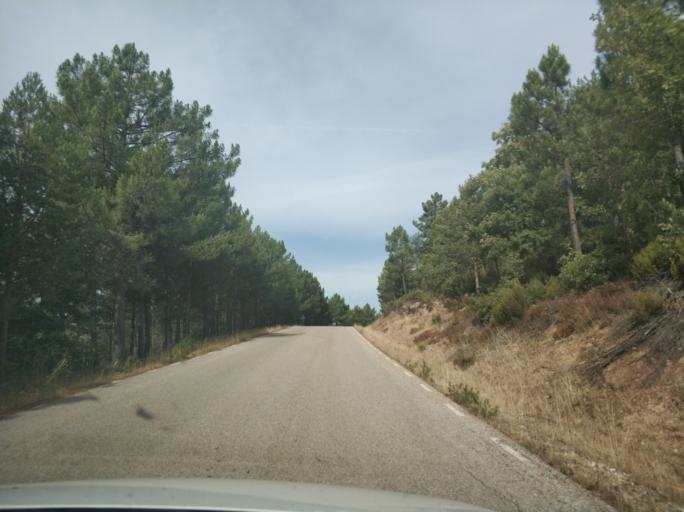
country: ES
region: Castille and Leon
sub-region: Provincia de Soria
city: Duruelo de la Sierra
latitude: 41.9009
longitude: -2.9397
